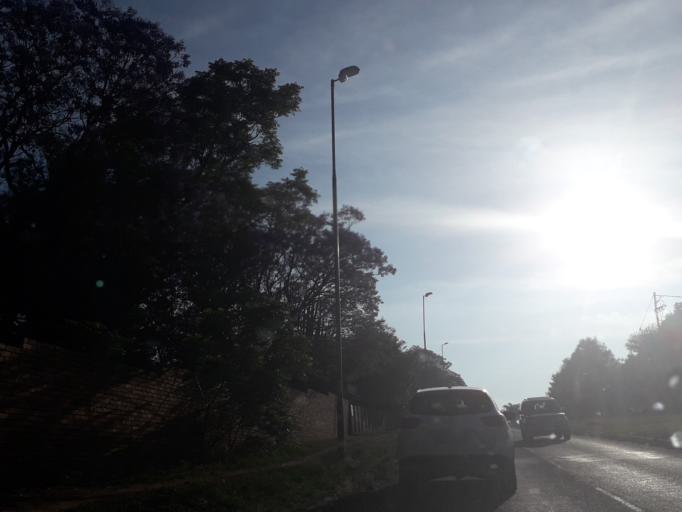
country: ZA
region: Gauteng
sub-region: City of Johannesburg Metropolitan Municipality
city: Roodepoort
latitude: -26.0984
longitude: 27.9151
